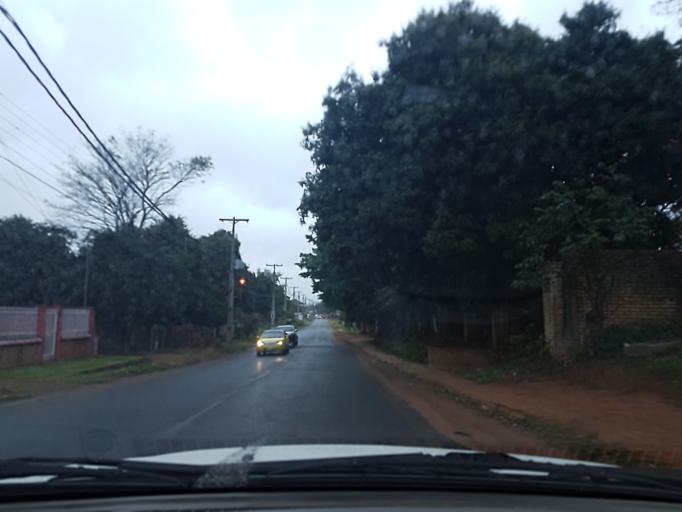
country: PY
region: Central
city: San Lorenzo
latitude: -25.2730
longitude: -57.4715
